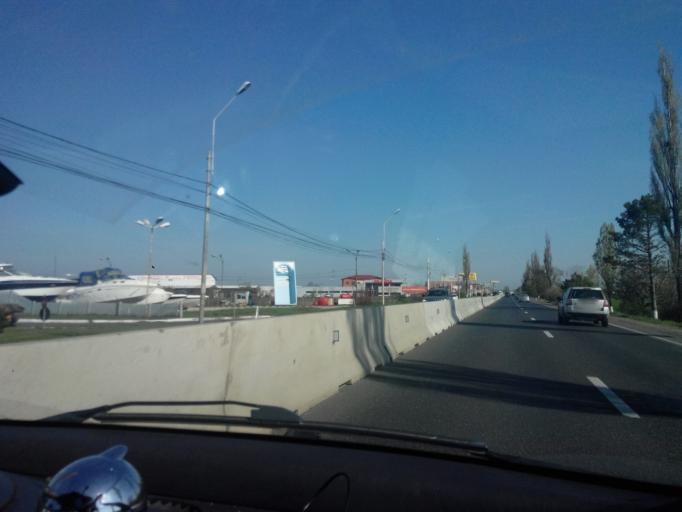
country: RO
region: Ilfov
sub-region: Comuna Corbeanca
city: Corbeanca
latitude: 44.5934
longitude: 26.0711
